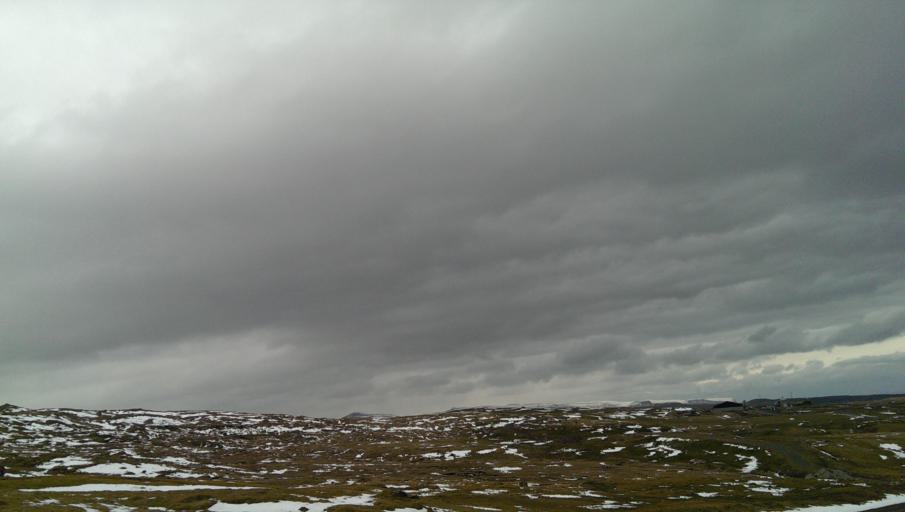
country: FO
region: Streymoy
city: Hoyvik
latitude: 62.0329
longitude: -6.8085
